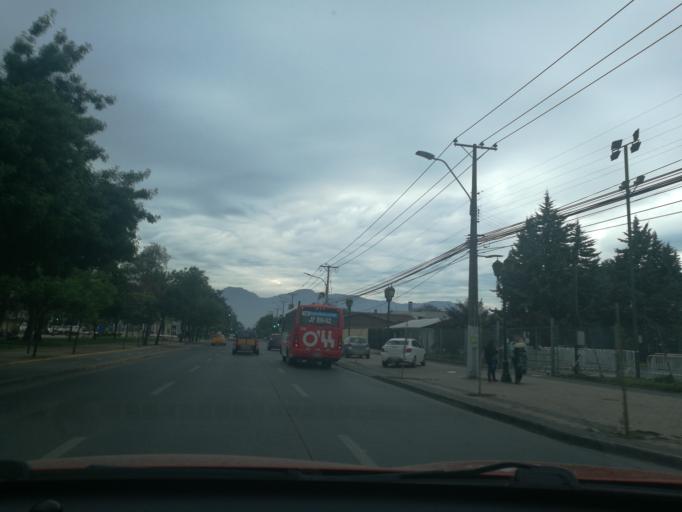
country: CL
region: O'Higgins
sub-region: Provincia de Cachapoal
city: Rancagua
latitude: -34.1656
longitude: -70.7370
